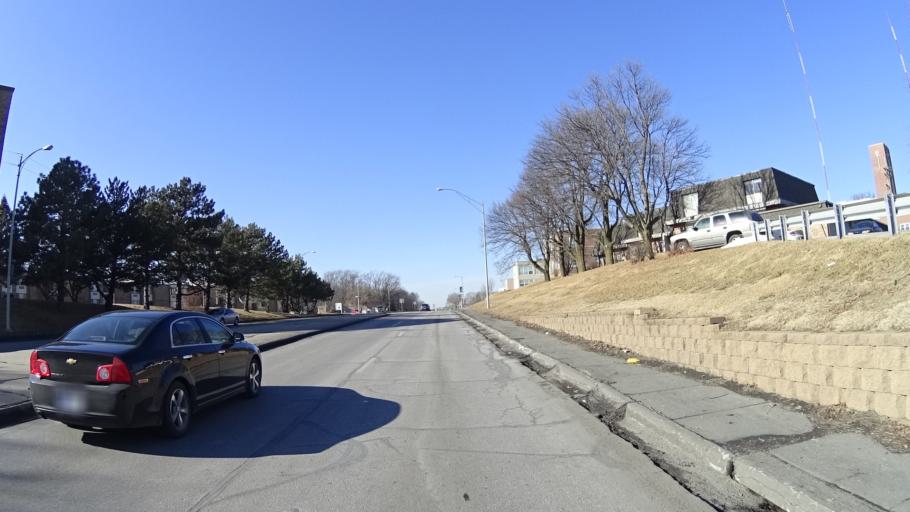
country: US
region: Nebraska
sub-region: Douglas County
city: Ralston
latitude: 41.2989
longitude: -96.0261
